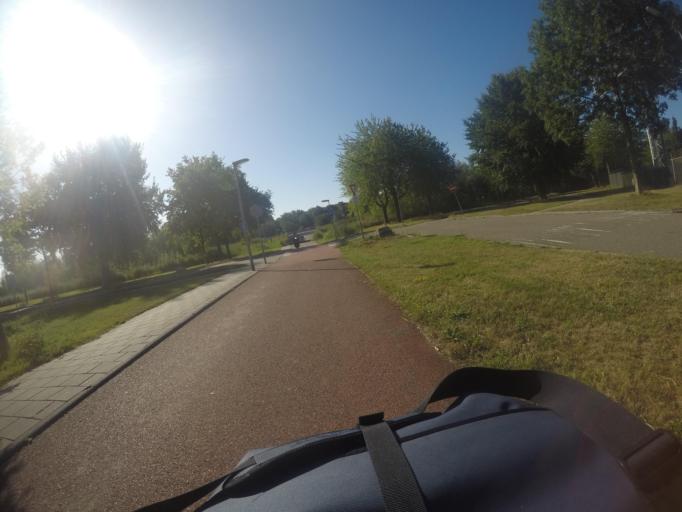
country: NL
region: Flevoland
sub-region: Gemeente Almere
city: Almere Stad
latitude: 52.3487
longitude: 5.1882
